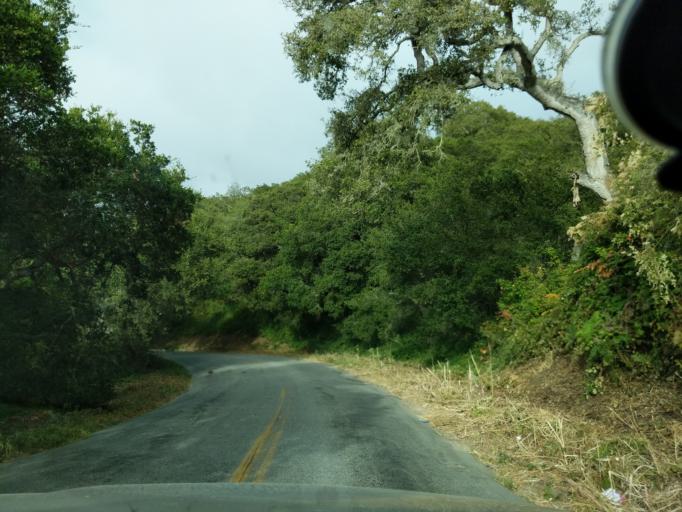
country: US
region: California
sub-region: Monterey County
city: Elkhorn
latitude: 36.8198
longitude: -121.7276
